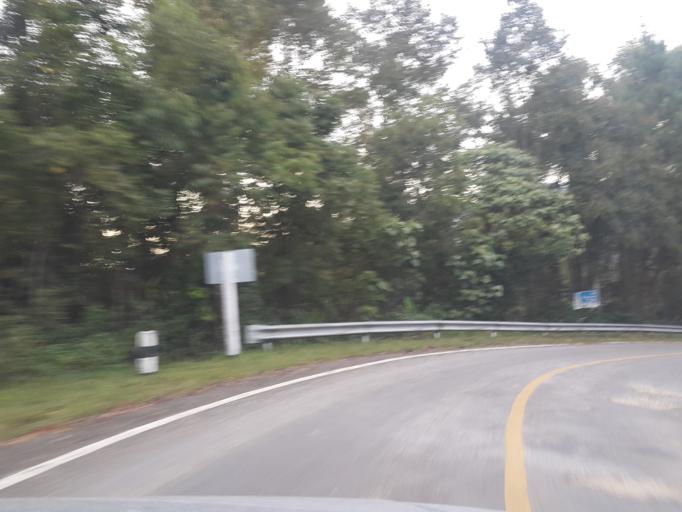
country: TH
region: Mae Hong Son
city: Khun Yuam
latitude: 18.8000
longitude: 98.0758
